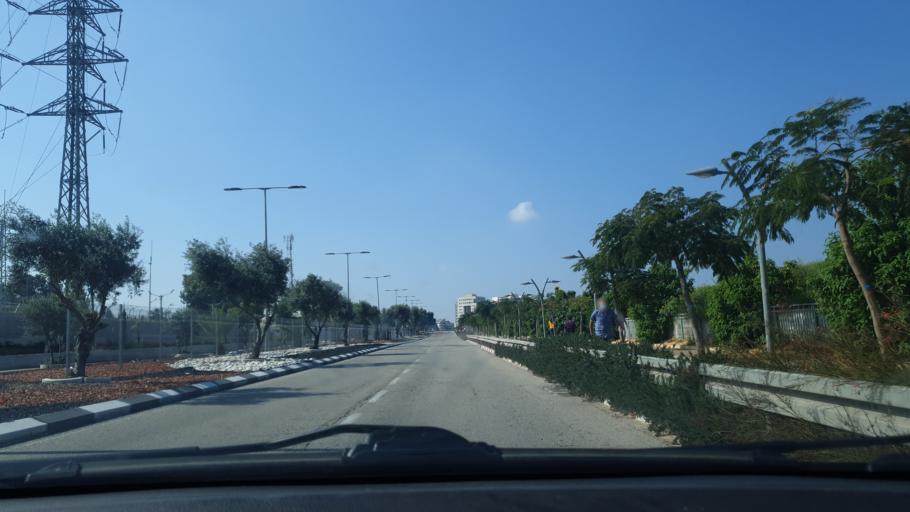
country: IL
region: Central District
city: Kefar Habad
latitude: 31.9705
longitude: 34.8320
